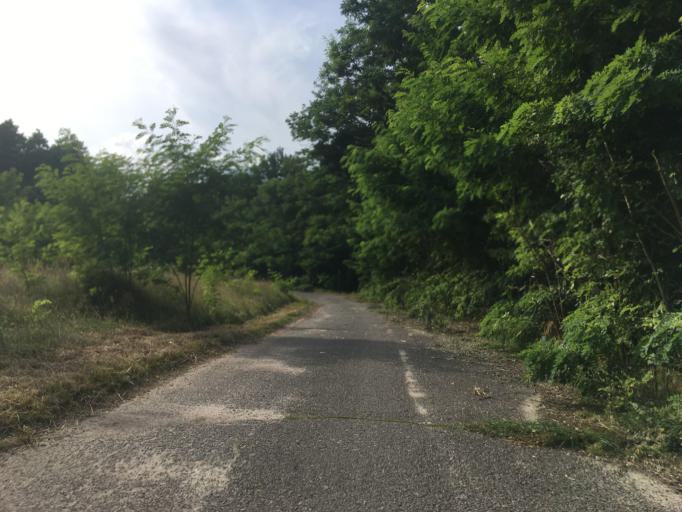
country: DE
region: Brandenburg
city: Eberswalde
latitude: 52.7865
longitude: 13.8230
